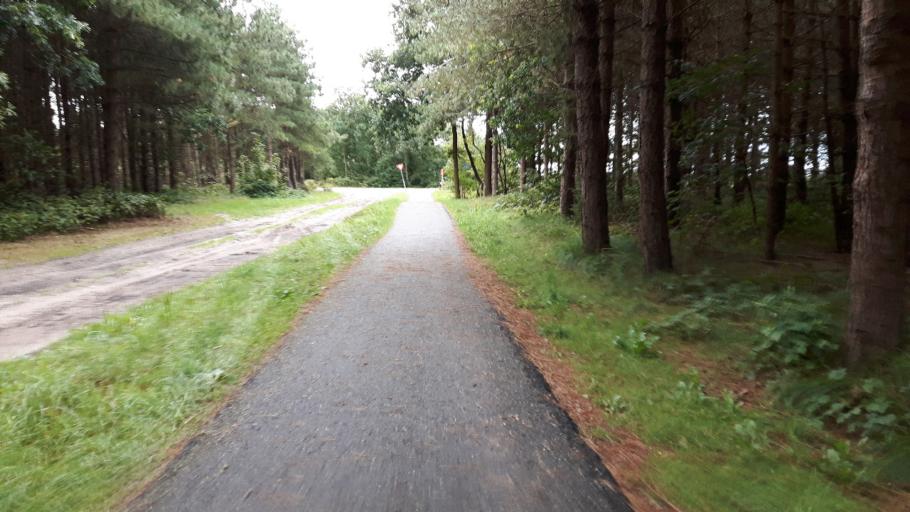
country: NL
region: Friesland
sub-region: Gemeente Ameland
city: Nes
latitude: 53.4467
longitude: 5.7122
